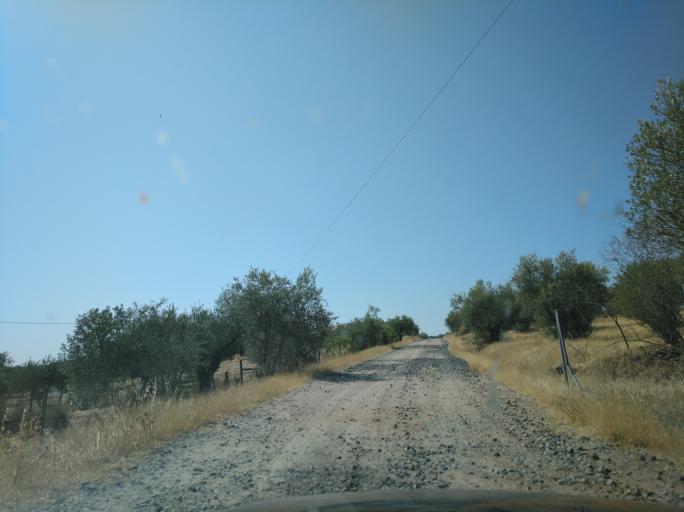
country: PT
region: Portalegre
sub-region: Campo Maior
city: Campo Maior
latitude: 39.0723
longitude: -7.0169
